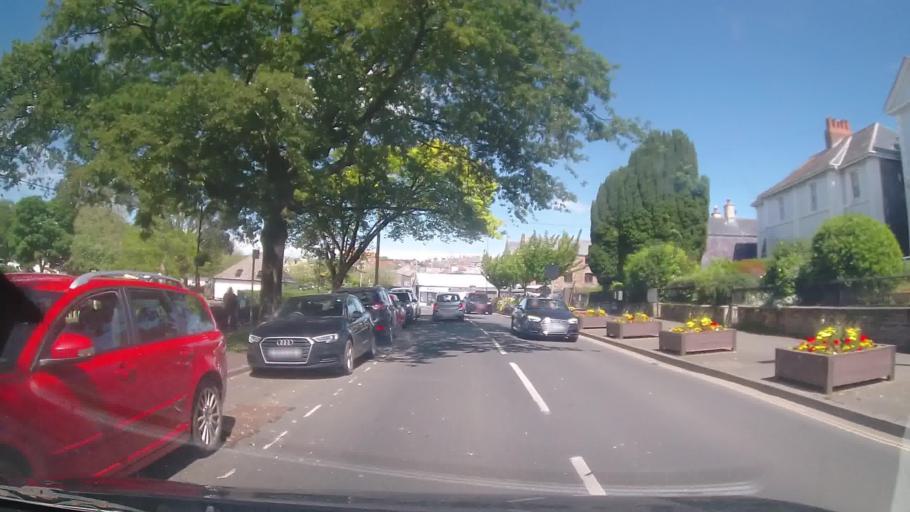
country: GB
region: England
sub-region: Devon
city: Kingsbridge
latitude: 50.2821
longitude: -3.7754
